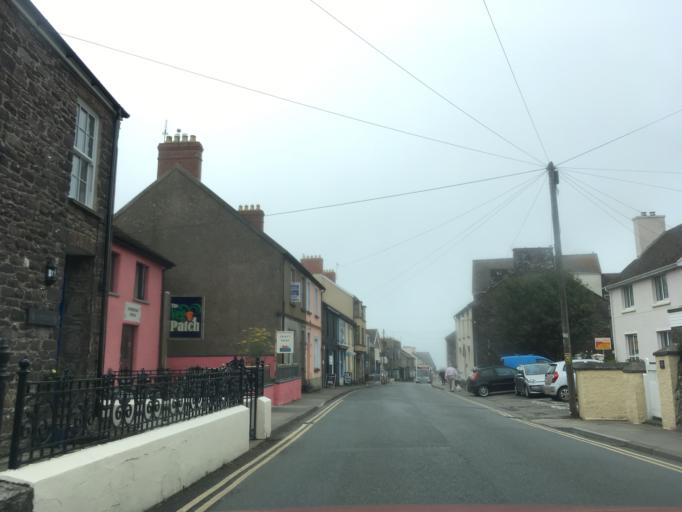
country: GB
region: Wales
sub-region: Pembrokeshire
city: Saint David's
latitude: 51.8807
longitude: -5.2627
